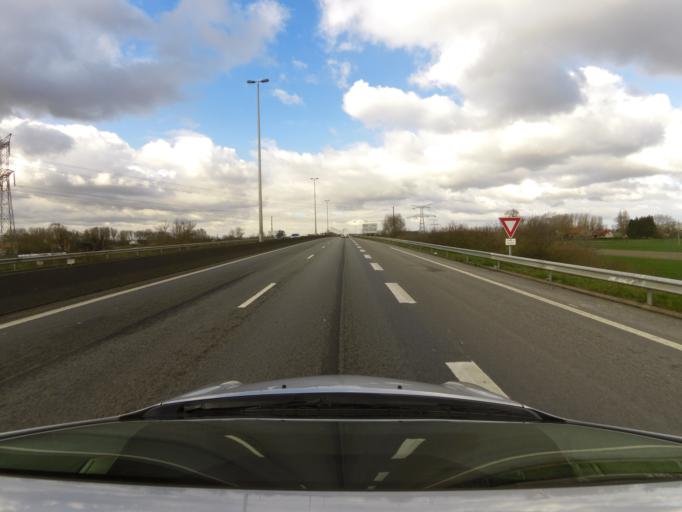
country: FR
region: Nord-Pas-de-Calais
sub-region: Departement du Pas-de-Calais
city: Saint-Folquin
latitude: 50.9543
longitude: 2.1402
